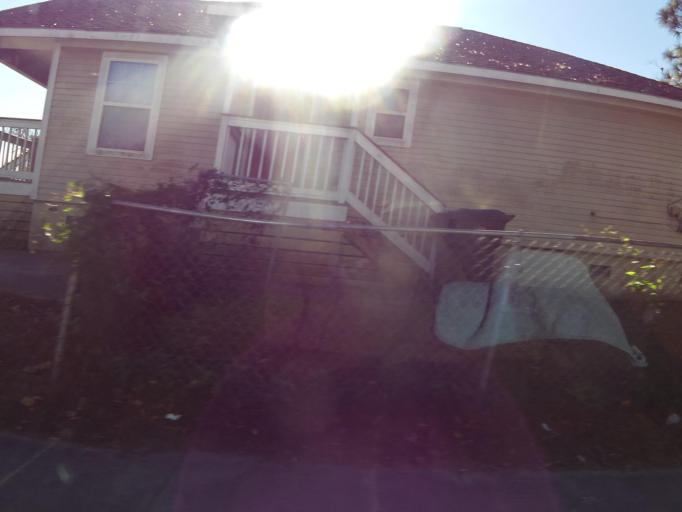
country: US
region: Georgia
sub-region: Chatham County
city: Savannah
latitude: 32.0731
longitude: -81.1186
